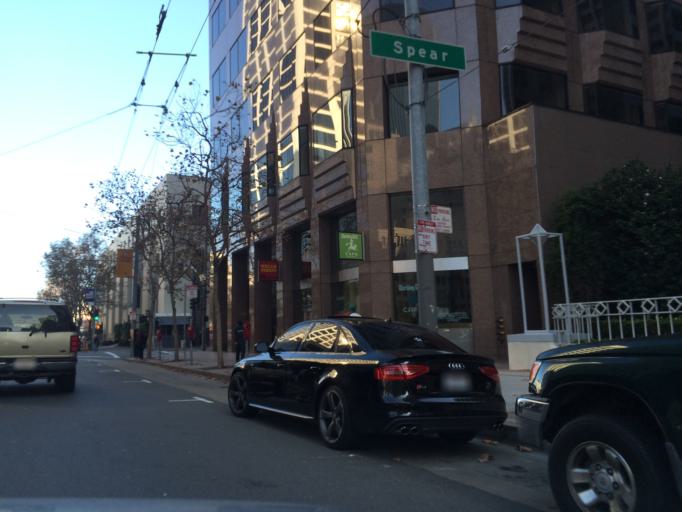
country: US
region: California
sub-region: San Francisco County
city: San Francisco
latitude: 37.7922
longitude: -122.3945
